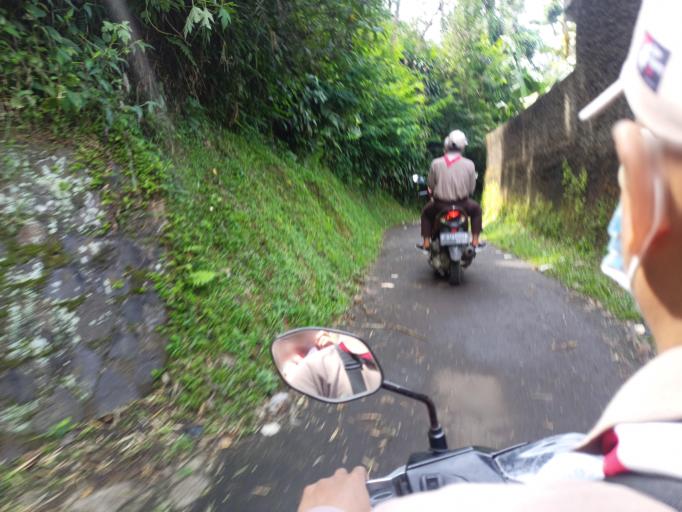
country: ID
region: West Java
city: Caringin
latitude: -6.6430
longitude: 106.9098
